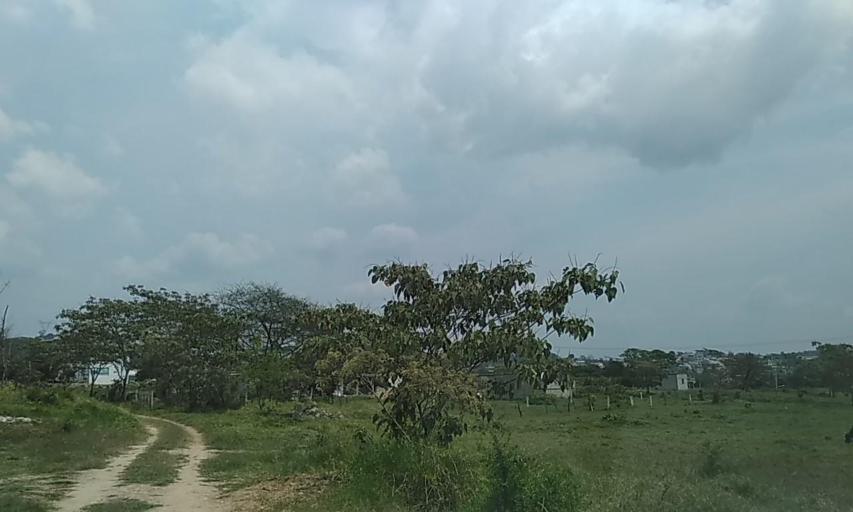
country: MX
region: Veracruz
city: El Castillo
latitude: 19.5424
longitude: -96.8780
